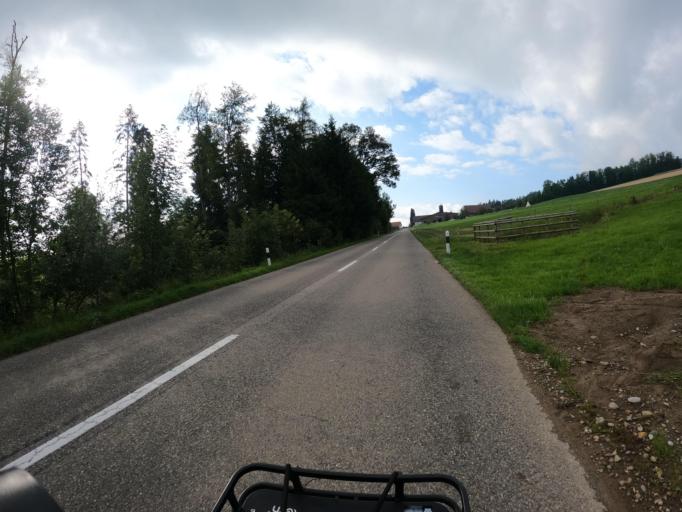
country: CH
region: Aargau
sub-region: Bezirk Muri
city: Buttwil
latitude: 47.2530
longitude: 8.3198
